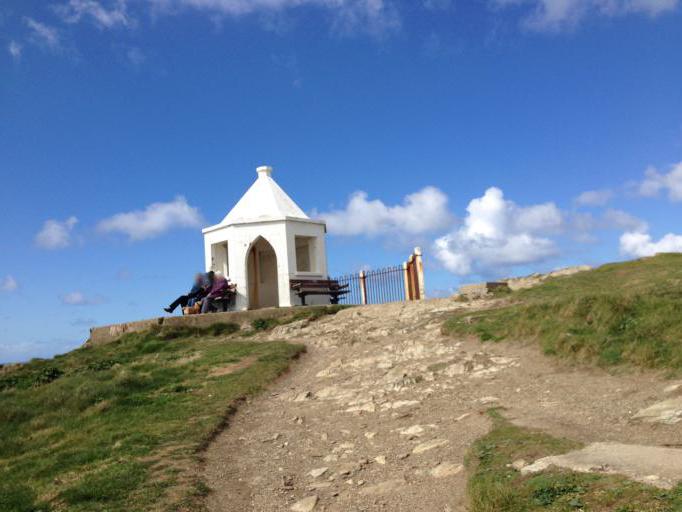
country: GB
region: England
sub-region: Cornwall
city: Newquay
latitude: 50.4251
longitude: -5.0992
